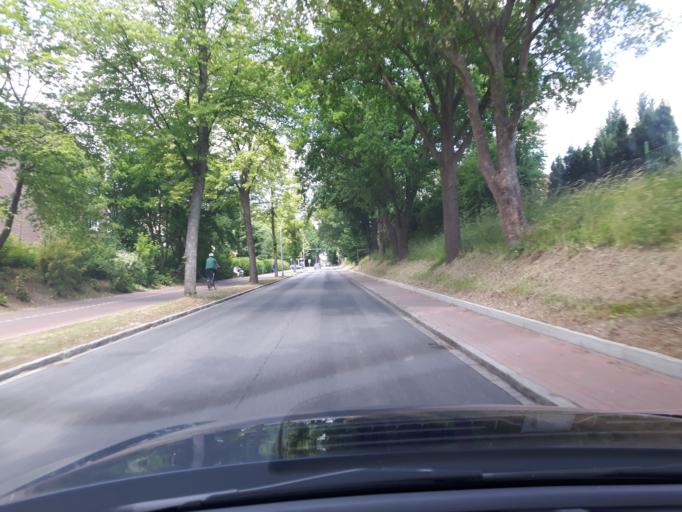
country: DE
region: Schleswig-Holstein
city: Neustadt in Holstein
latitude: 54.0948
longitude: 10.8240
